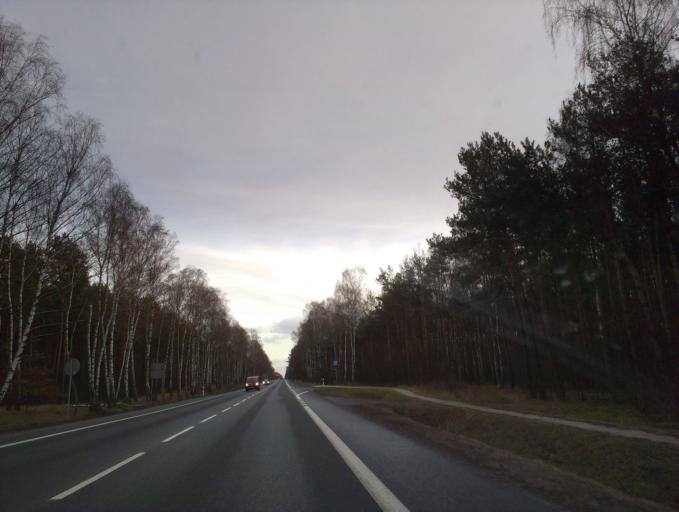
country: PL
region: Masovian Voivodeship
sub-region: Powiat sierpecki
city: Szczutowo
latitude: 52.8907
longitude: 19.5658
